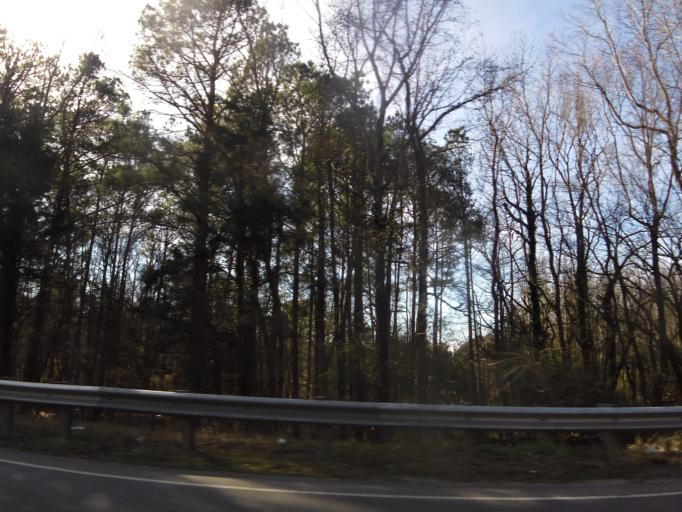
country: US
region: Virginia
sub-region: Isle of Wight County
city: Smithfield
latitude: 36.9753
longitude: -76.6395
